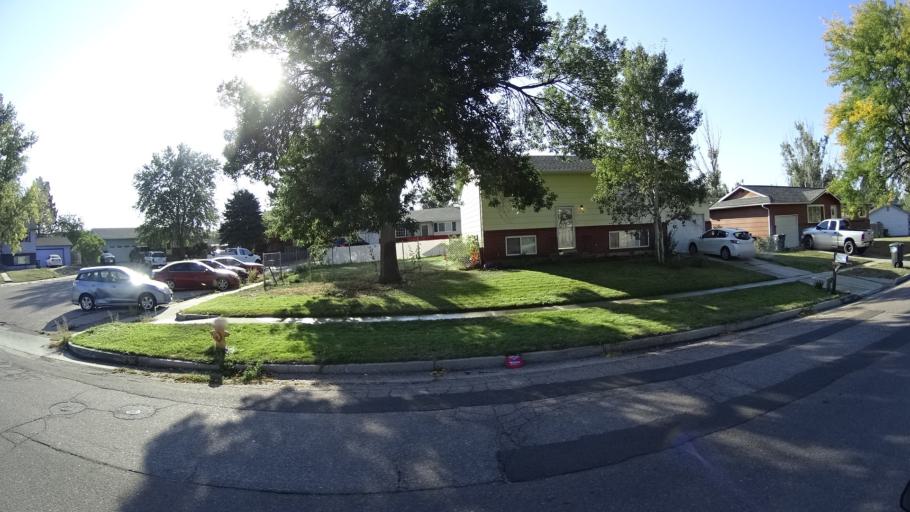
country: US
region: Colorado
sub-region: El Paso County
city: Cimarron Hills
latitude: 38.8929
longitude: -104.7469
